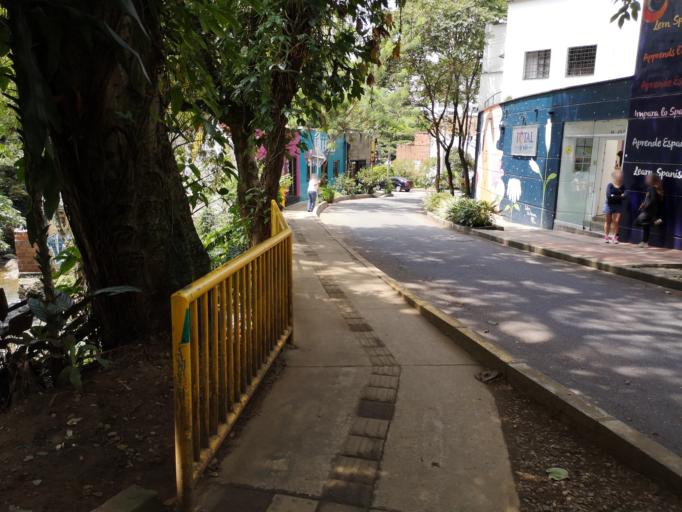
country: CO
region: Antioquia
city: Itagui
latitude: 6.2074
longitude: -75.5673
